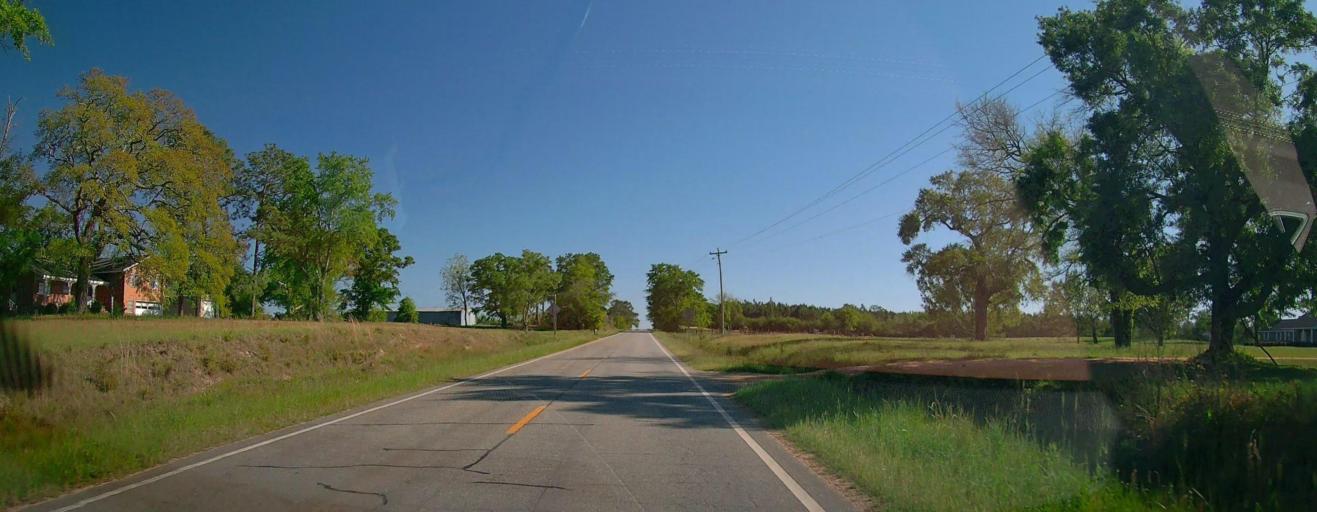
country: US
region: Georgia
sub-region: Wilcox County
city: Rochelle
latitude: 31.8941
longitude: -83.4888
